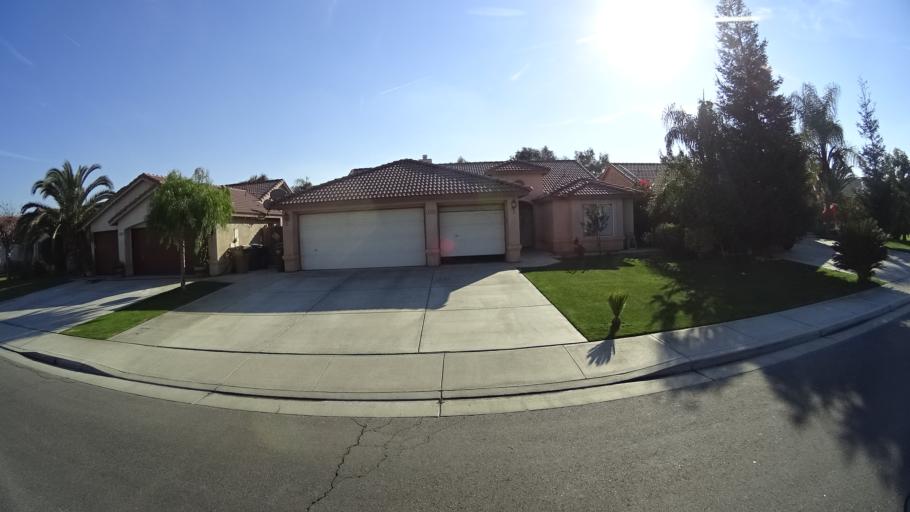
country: US
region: California
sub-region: Kern County
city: Greenfield
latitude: 35.2864
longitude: -119.0559
